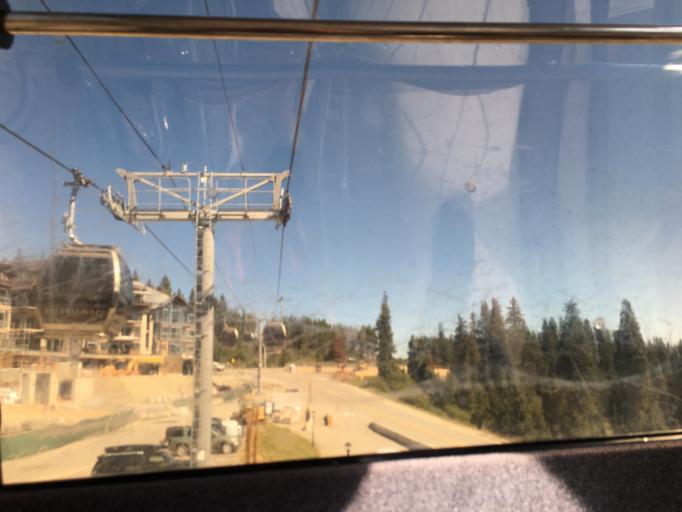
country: US
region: Colorado
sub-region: Summit County
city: Breckenridge
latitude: 39.4813
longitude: -106.0669
